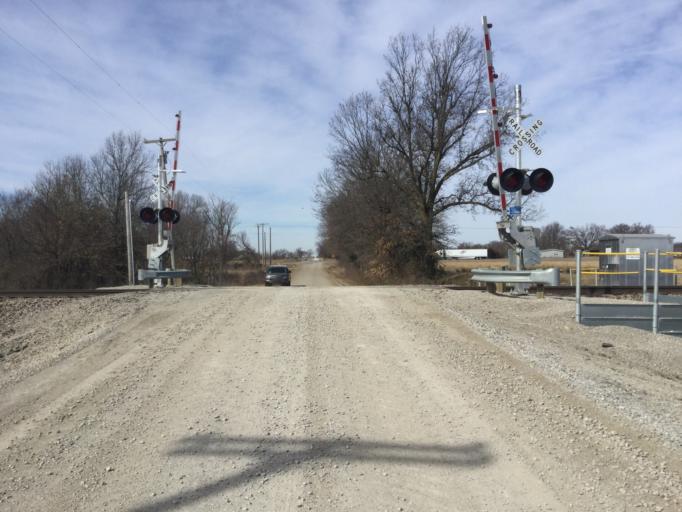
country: US
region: Kansas
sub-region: Cherokee County
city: Columbus
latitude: 37.2078
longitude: -94.8292
